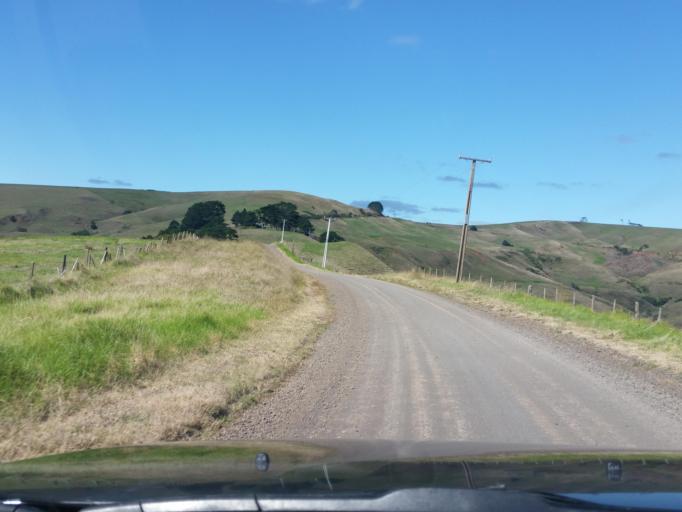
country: NZ
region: Northland
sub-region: Kaipara District
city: Dargaville
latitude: -35.7187
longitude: 173.5549
